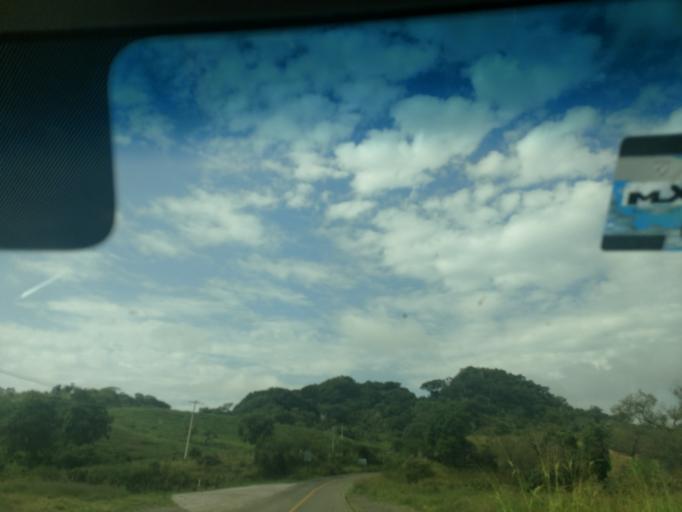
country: MX
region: Jalisco
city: El Salto
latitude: 20.4181
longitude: -104.5003
